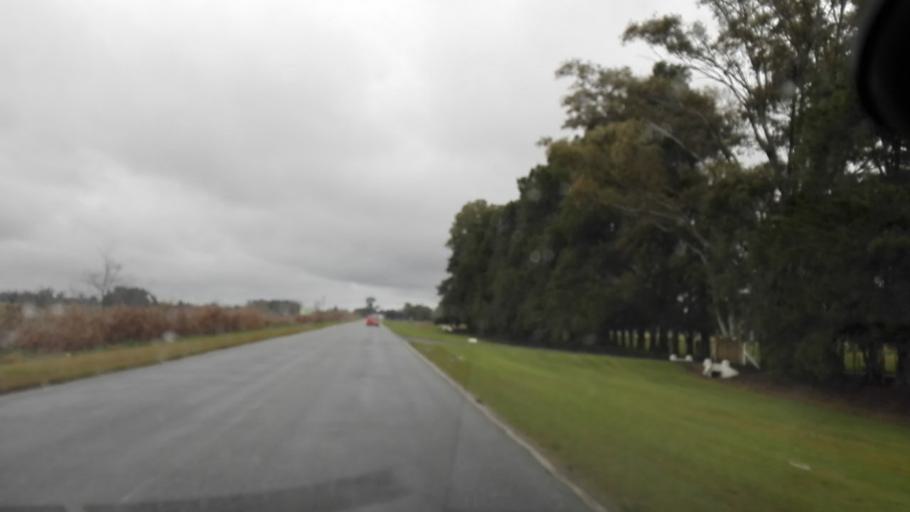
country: AR
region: Buenos Aires
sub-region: Partido de Brandsen
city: Brandsen
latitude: -35.1774
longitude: -58.2860
